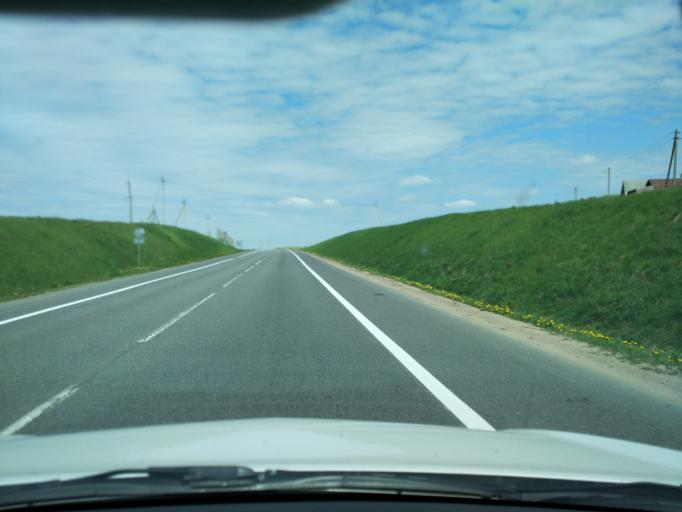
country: BY
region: Grodnenskaya
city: Ashmyany
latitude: 54.4413
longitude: 25.9679
